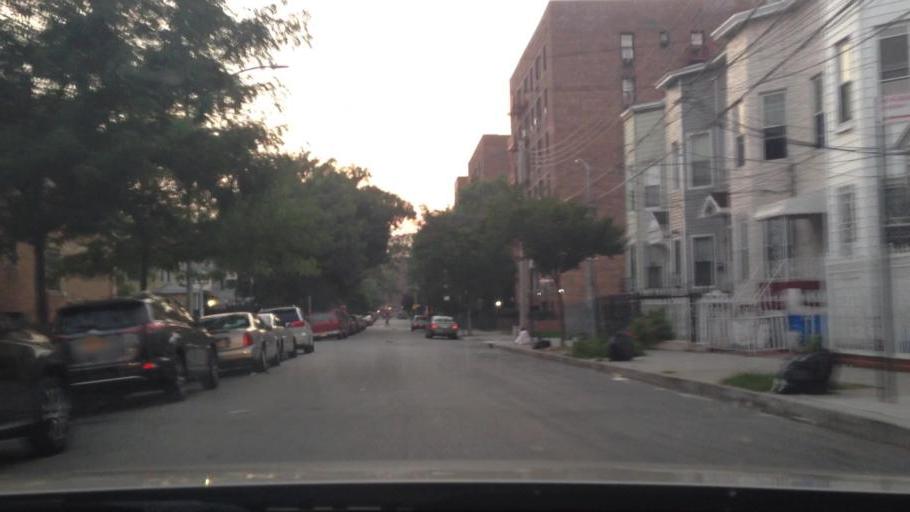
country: US
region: New York
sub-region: Queens County
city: Jamaica
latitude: 40.7095
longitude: -73.7941
